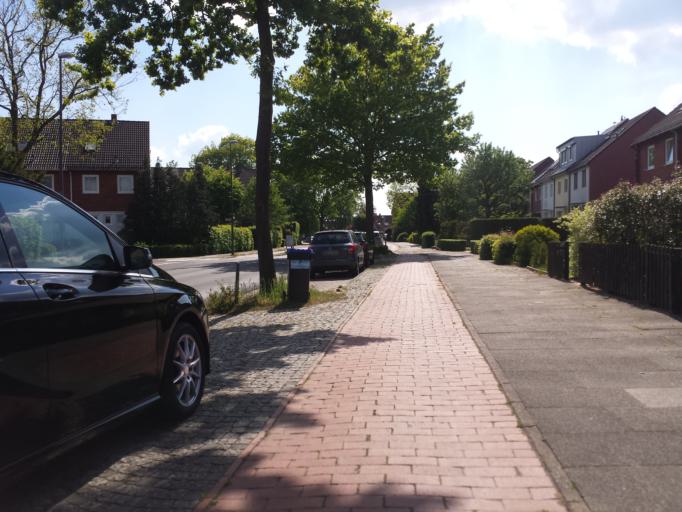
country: DE
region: Lower Saxony
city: Lilienthal
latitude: 53.1151
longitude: 8.8974
